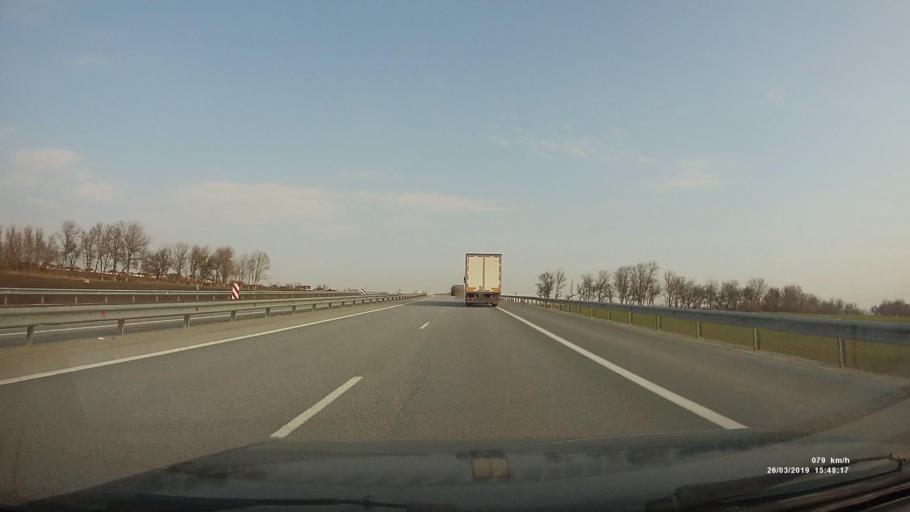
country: RU
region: Rostov
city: Chaltyr
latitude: 47.2790
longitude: 39.4506
